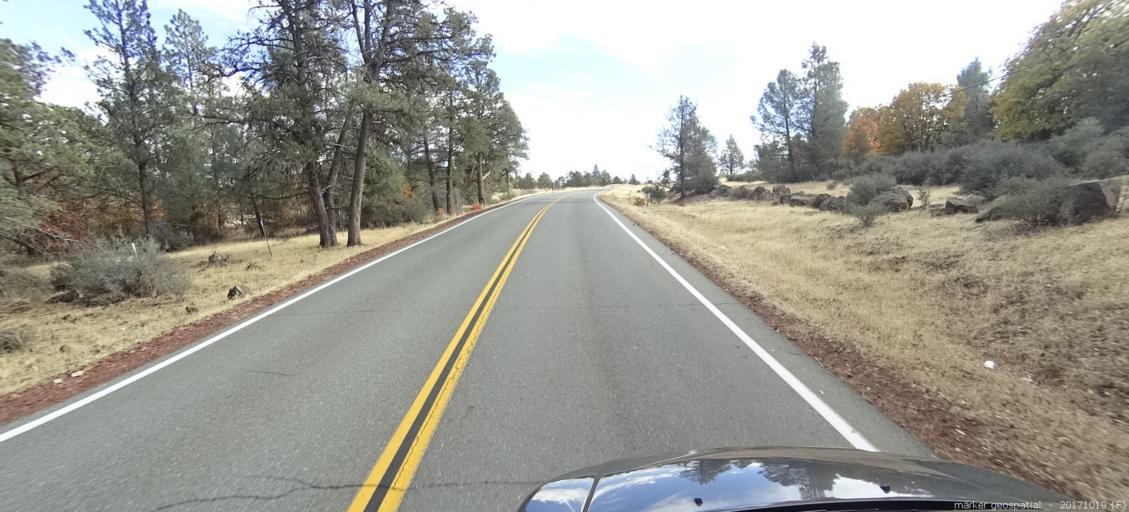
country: US
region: California
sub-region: Shasta County
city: Burney
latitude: 40.9941
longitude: -121.4306
